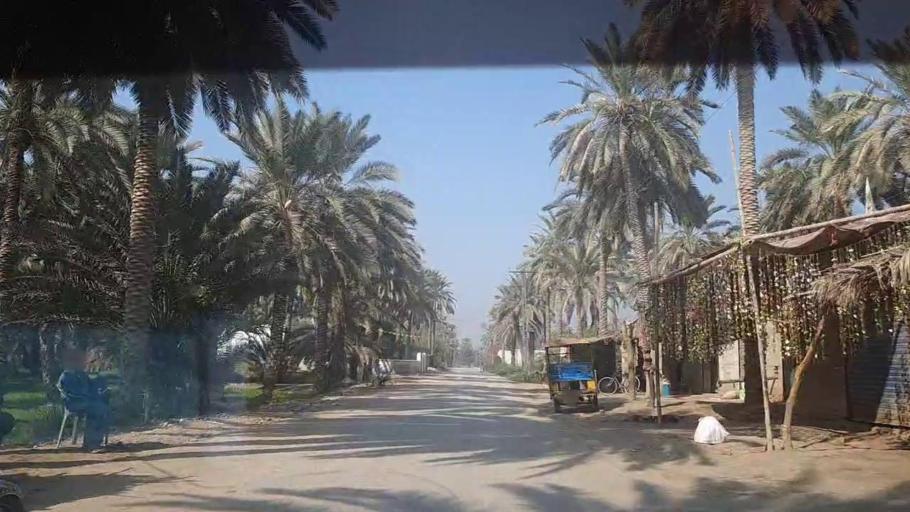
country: PK
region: Sindh
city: Kot Diji
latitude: 27.3789
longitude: 68.6912
